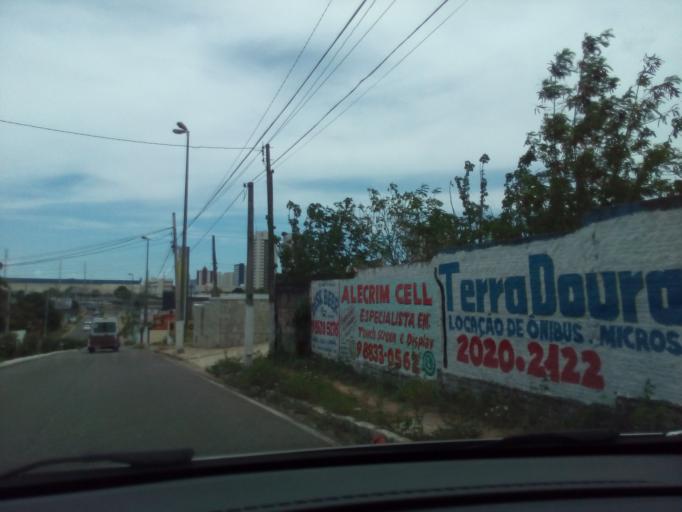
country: BR
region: Rio Grande do Norte
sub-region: Natal
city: Natal
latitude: -5.8487
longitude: -35.2118
